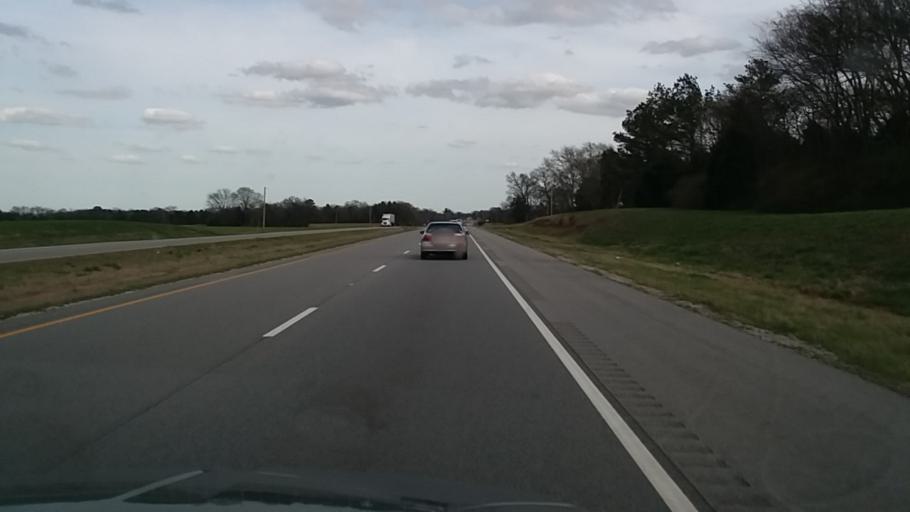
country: US
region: Alabama
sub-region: Lawrence County
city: Town Creek
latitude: 34.6824
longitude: -87.4633
